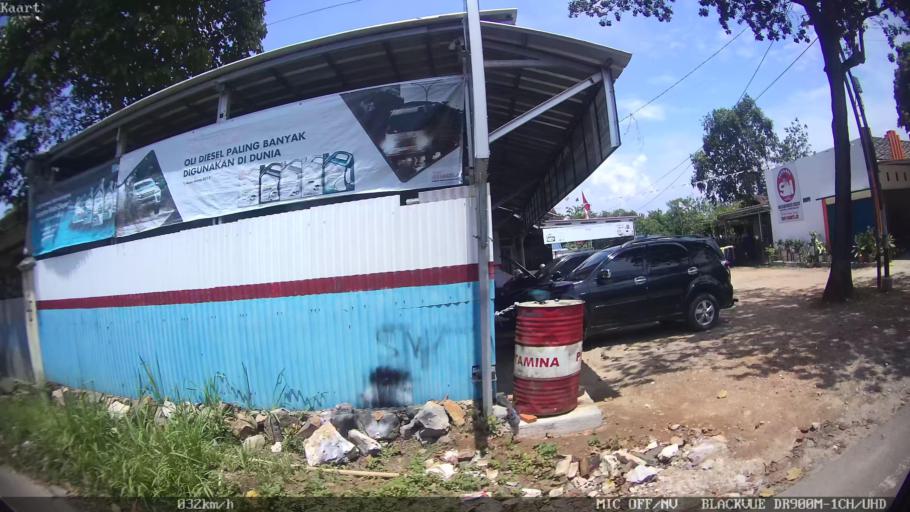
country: ID
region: Lampung
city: Kedaton
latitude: -5.3605
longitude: 105.2896
